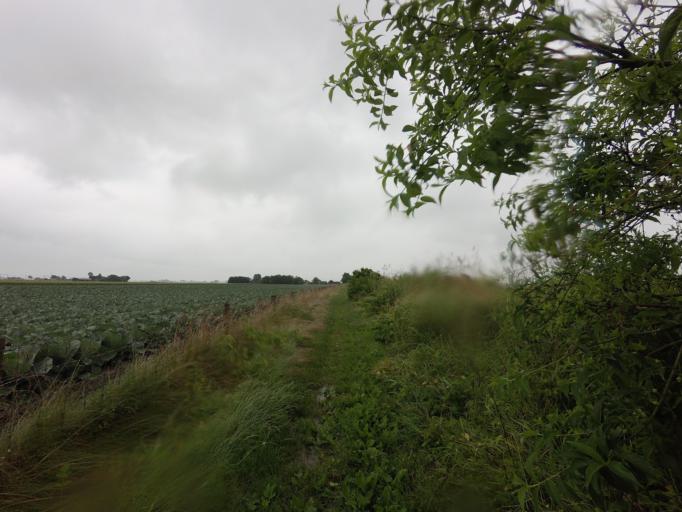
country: NL
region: North Holland
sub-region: Gemeente Schagen
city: Schagen
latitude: 52.7684
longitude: 4.8004
